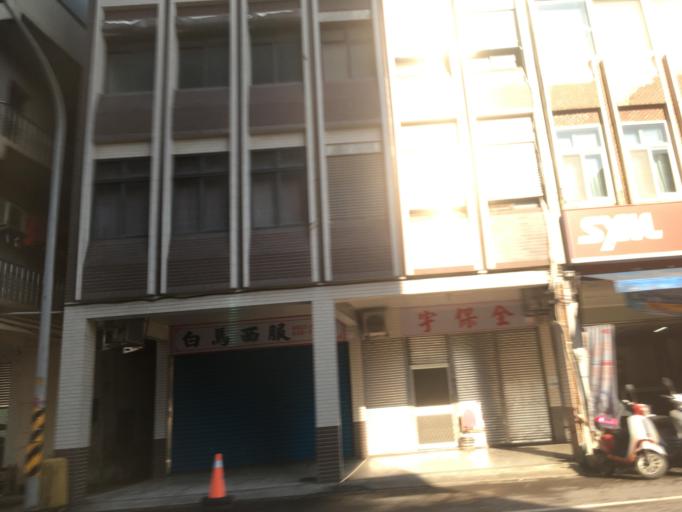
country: TW
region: Taiwan
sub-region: Yilan
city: Yilan
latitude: 24.8552
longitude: 121.8233
